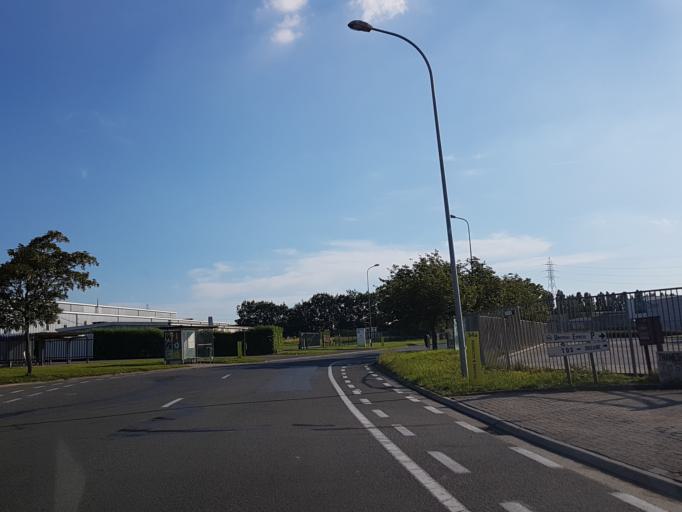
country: BE
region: Flanders
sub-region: Provincie Oost-Vlaanderen
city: Aalst
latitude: 50.9607
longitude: 4.0455
